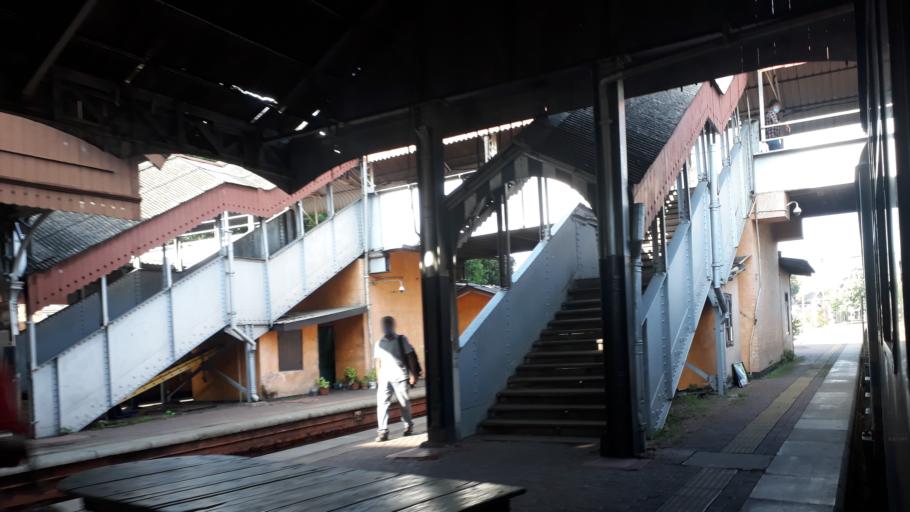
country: LK
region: Western
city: Colombo
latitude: 6.9334
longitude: 79.8511
